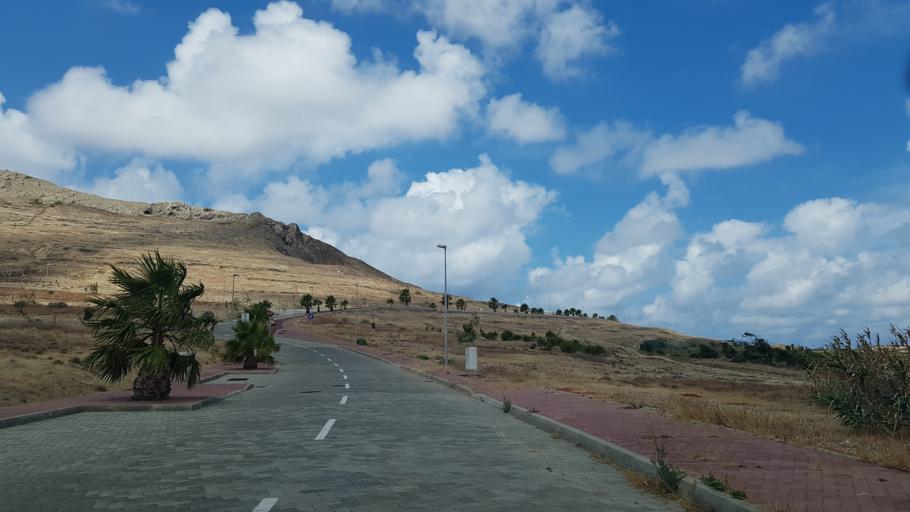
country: PT
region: Madeira
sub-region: Porto Santo
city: Vila de Porto Santo
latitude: 33.0500
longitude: -16.3638
